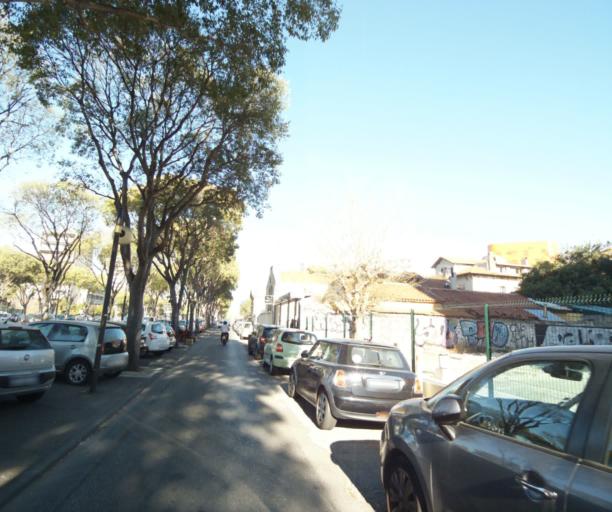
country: FR
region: Provence-Alpes-Cote d'Azur
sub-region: Departement des Bouches-du-Rhone
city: Marseille 08
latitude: 43.2669
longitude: 5.3947
